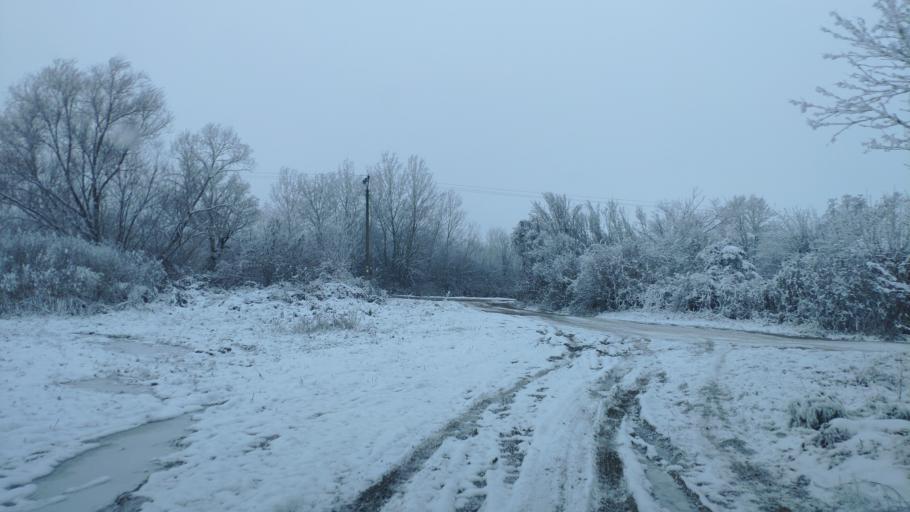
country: SK
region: Kosicky
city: Kosice
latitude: 48.6487
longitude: 21.1688
